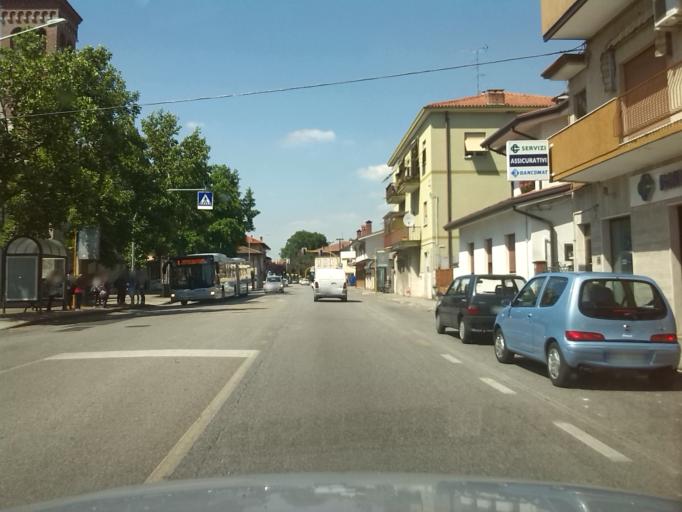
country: IT
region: Friuli Venezia Giulia
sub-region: Provincia di Gorizia
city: Fogliano
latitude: 45.8646
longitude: 13.4821
